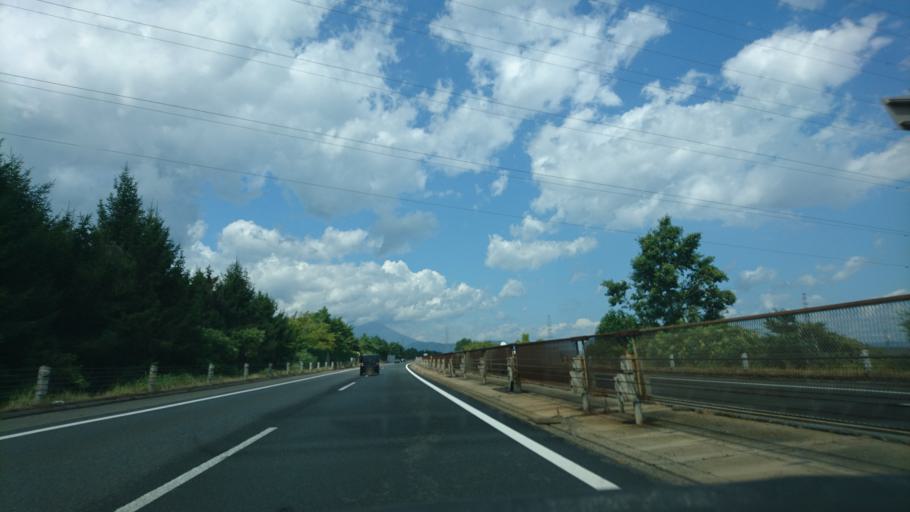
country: JP
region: Iwate
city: Morioka-shi
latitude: 39.6751
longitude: 141.1047
